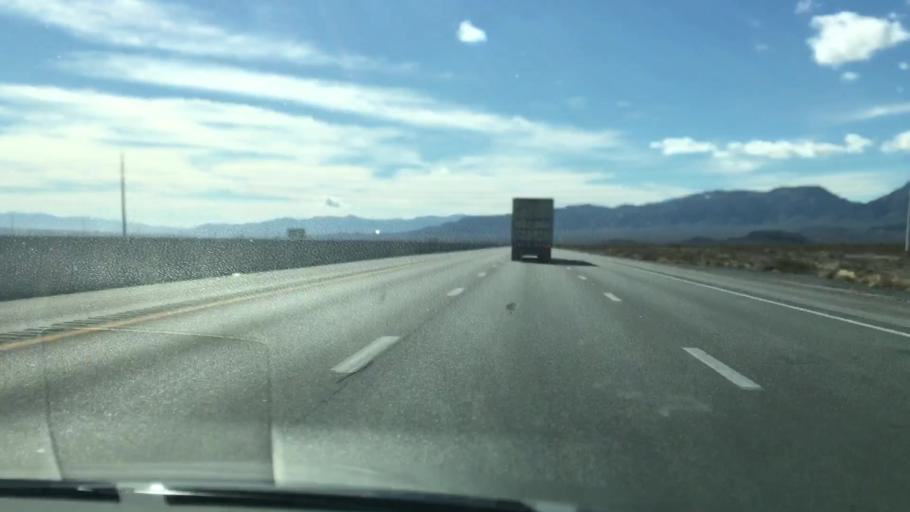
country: US
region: Nevada
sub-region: Clark County
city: Enterprise
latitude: 35.7652
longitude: -115.3401
